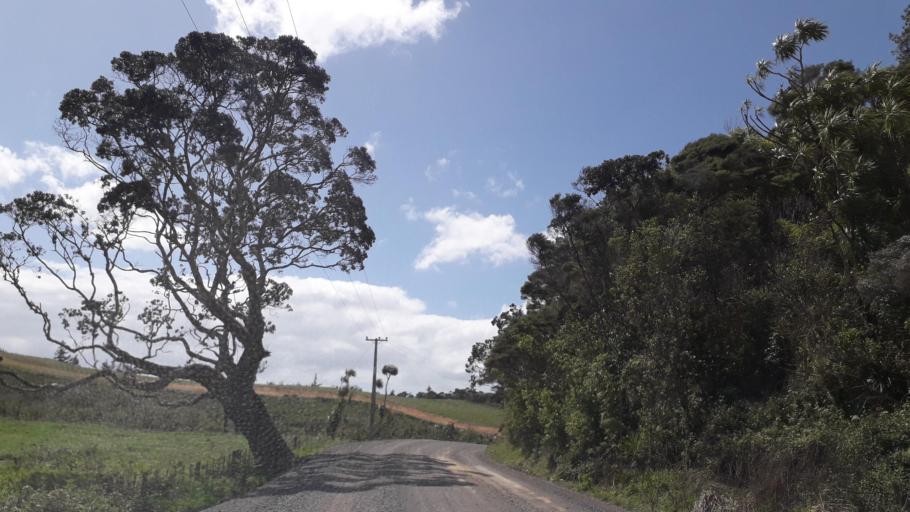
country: NZ
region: Northland
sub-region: Far North District
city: Paihia
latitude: -35.2401
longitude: 174.2482
